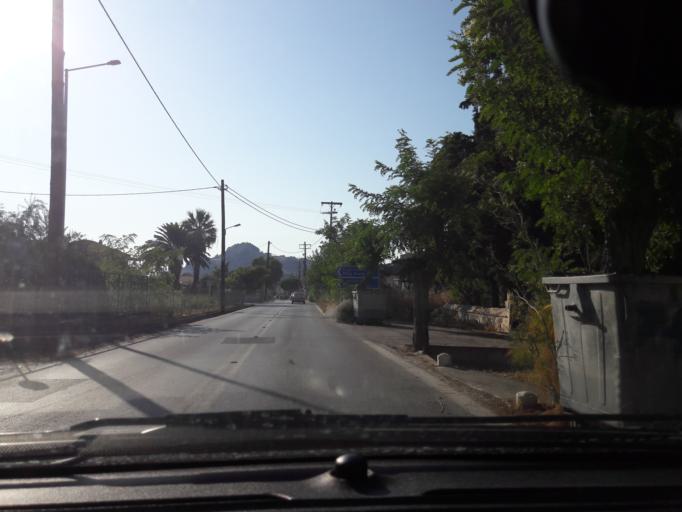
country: GR
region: North Aegean
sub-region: Nomos Lesvou
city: Myrina
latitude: 39.8708
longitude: 25.0690
